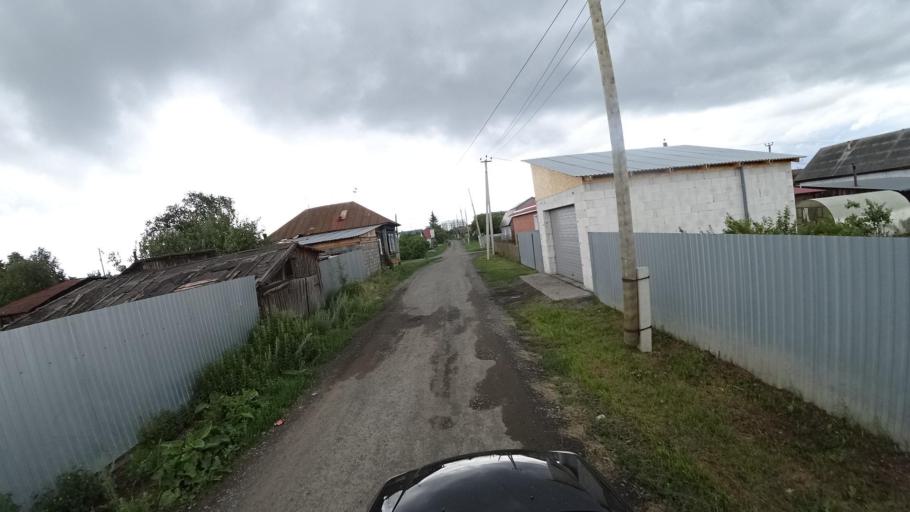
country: RU
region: Sverdlovsk
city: Kamyshlov
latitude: 56.8534
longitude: 62.6879
